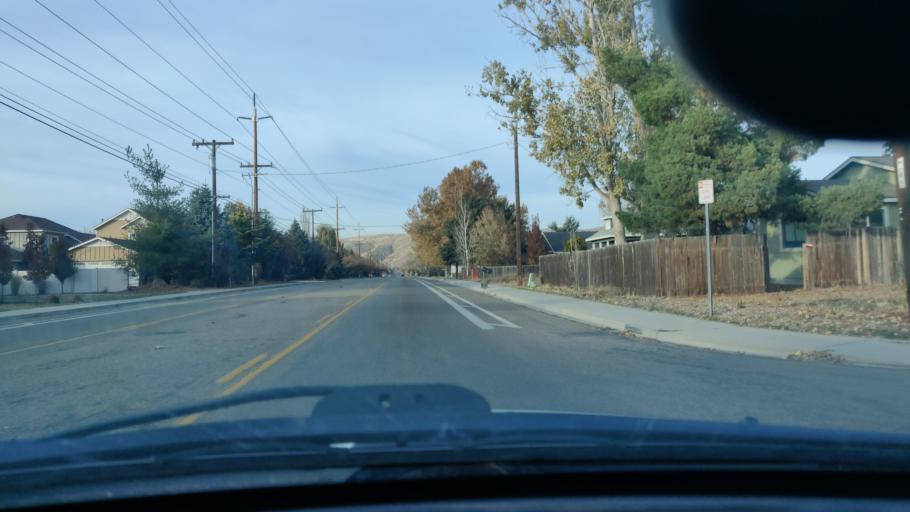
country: US
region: Idaho
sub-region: Ada County
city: Garden City
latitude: 43.6725
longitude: -116.2792
